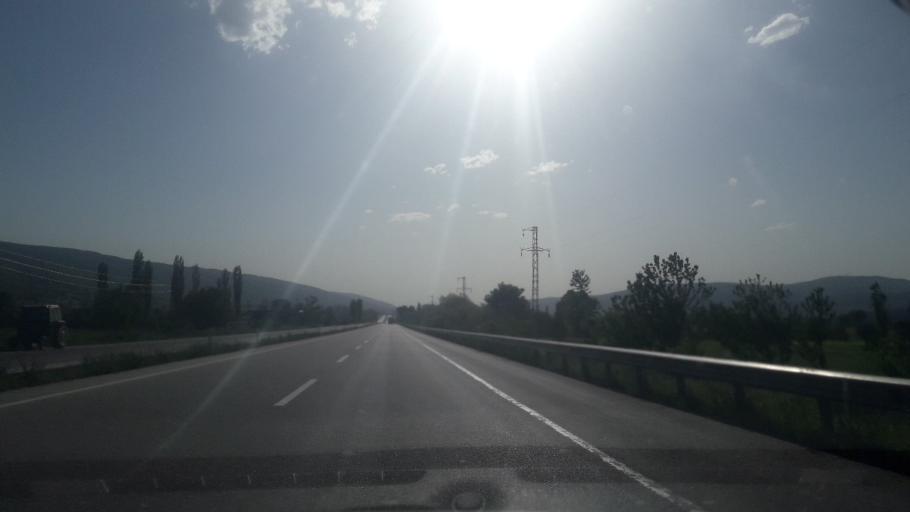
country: TR
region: Amasya
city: Ezinepazari
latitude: 40.5712
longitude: 36.1005
